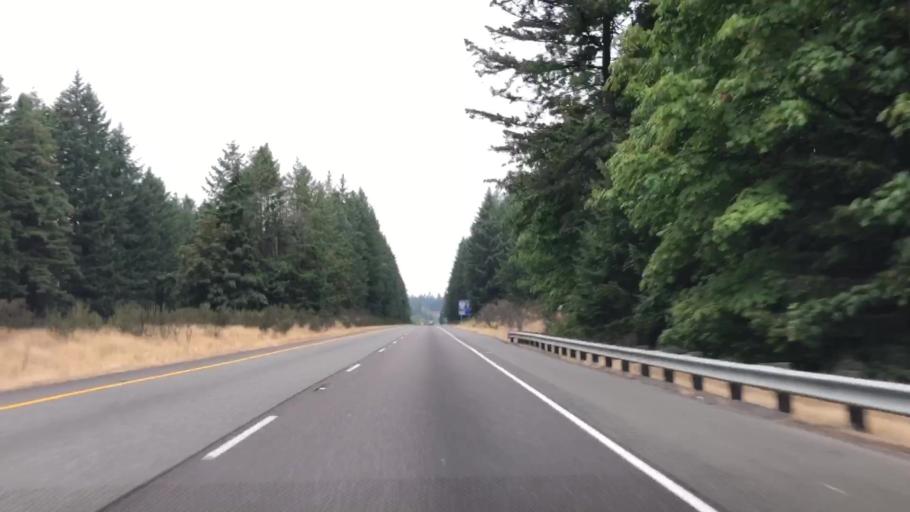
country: US
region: Washington
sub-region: Kitsap County
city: Bethel
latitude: 47.4939
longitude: -122.6383
